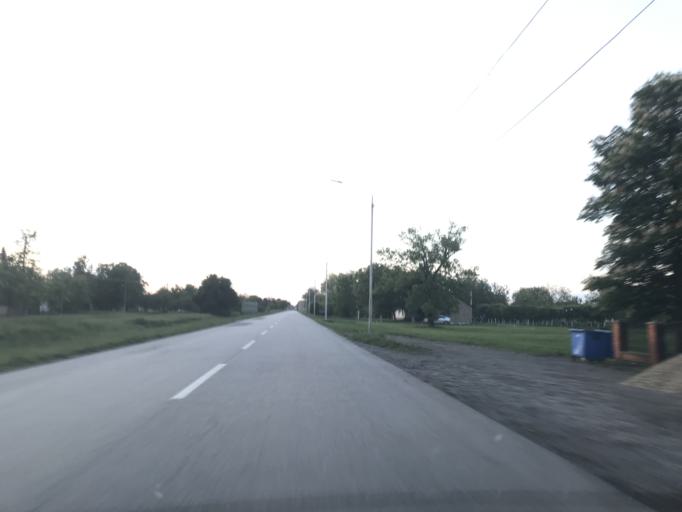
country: RS
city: Srpska Crnja
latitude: 45.7403
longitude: 20.6991
